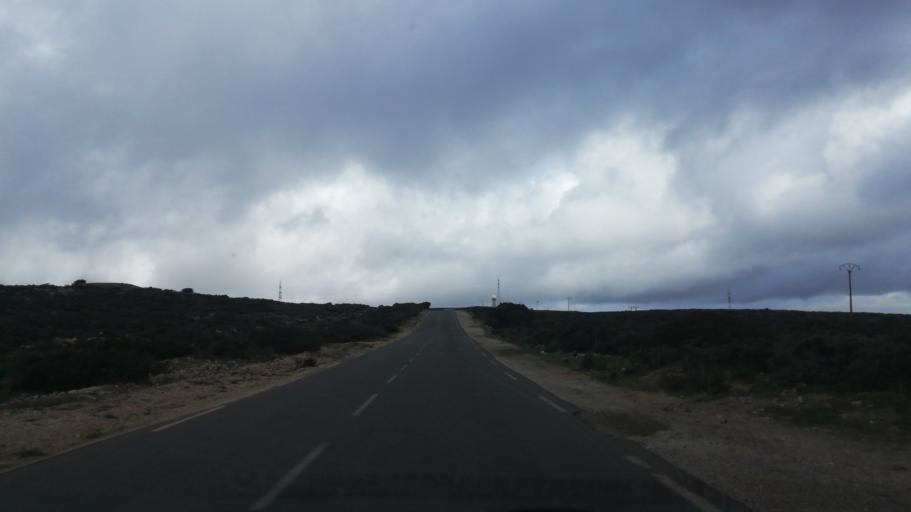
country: DZ
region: Oran
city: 'Ain el Turk
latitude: 35.6872
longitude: -0.7844
